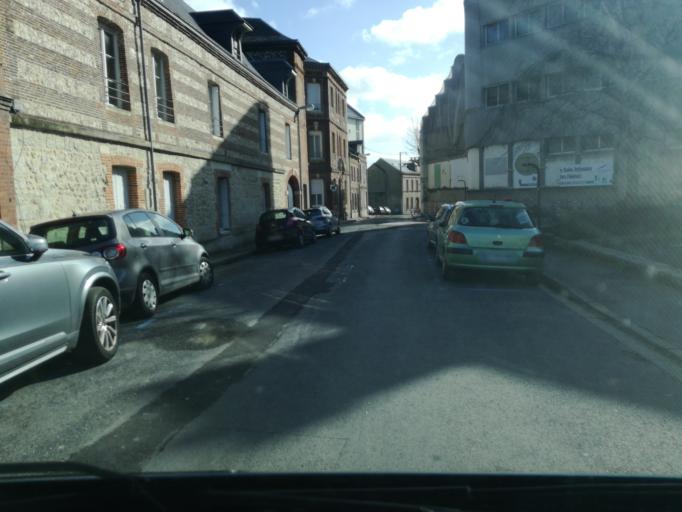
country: FR
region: Haute-Normandie
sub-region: Departement de la Seine-Maritime
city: Fecamp
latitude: 49.7580
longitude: 0.3791
